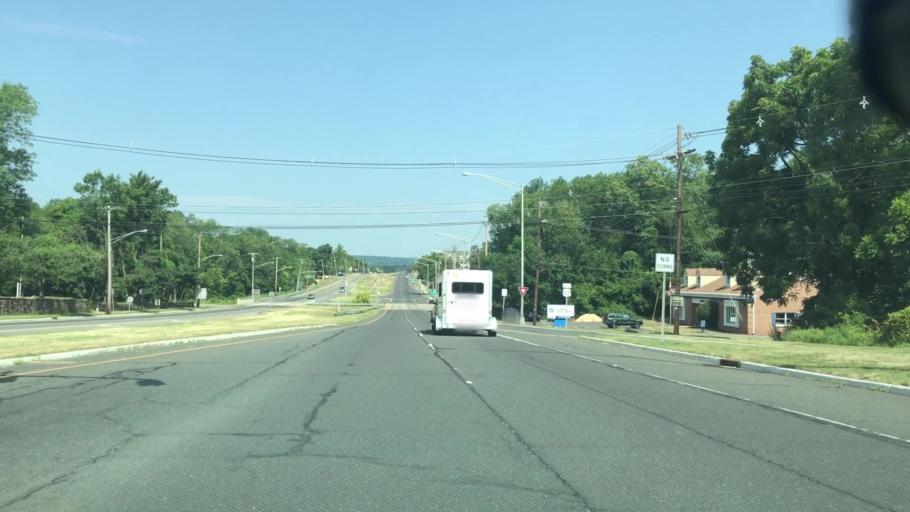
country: US
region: New Jersey
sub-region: Hunterdon County
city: Whitehouse Station
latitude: 40.6223
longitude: -74.7648
